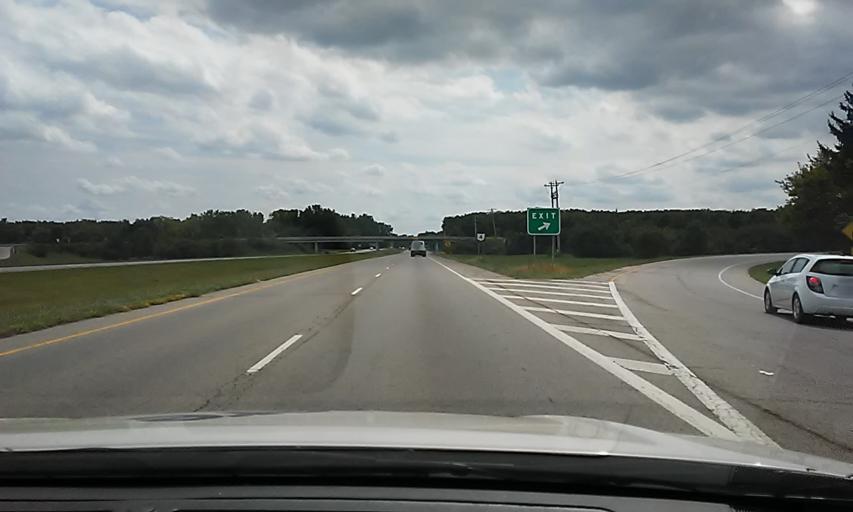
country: US
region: Ohio
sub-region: Greene County
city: Wright-Patterson AFB
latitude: 39.8463
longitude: -84.0588
